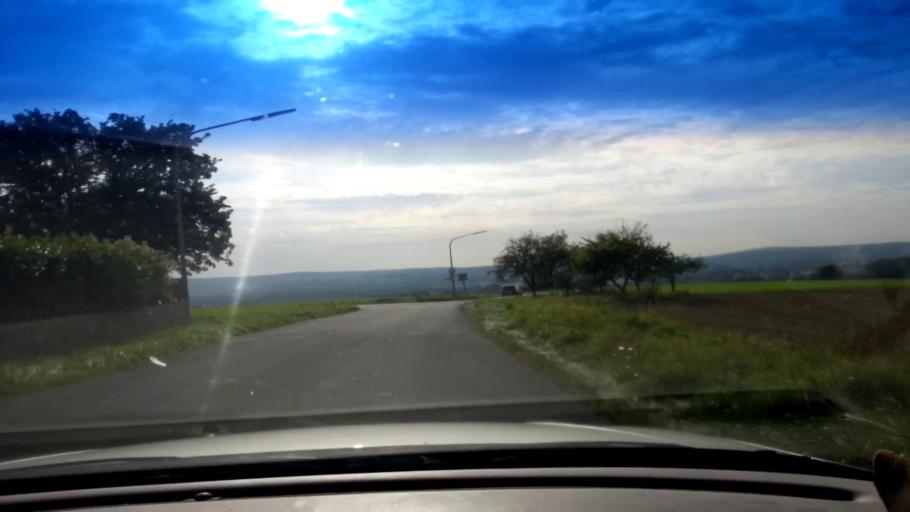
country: DE
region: Bavaria
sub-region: Upper Franconia
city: Buttenheim
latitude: 49.8216
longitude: 11.0218
